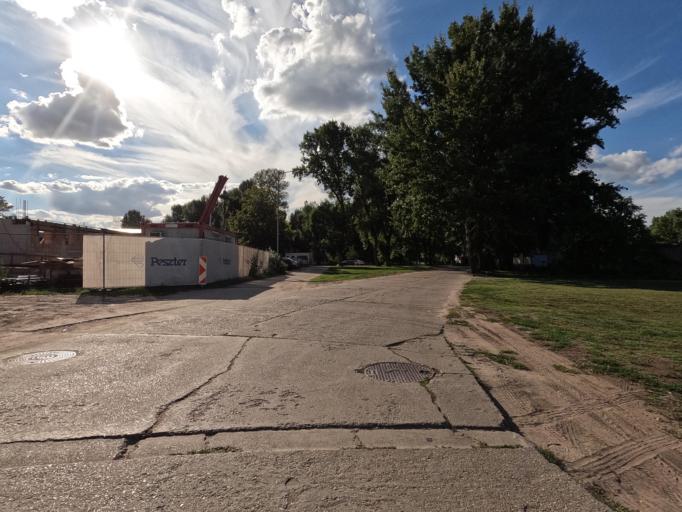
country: HU
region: Tolna
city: Paks
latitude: 46.6174
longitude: 18.8352
